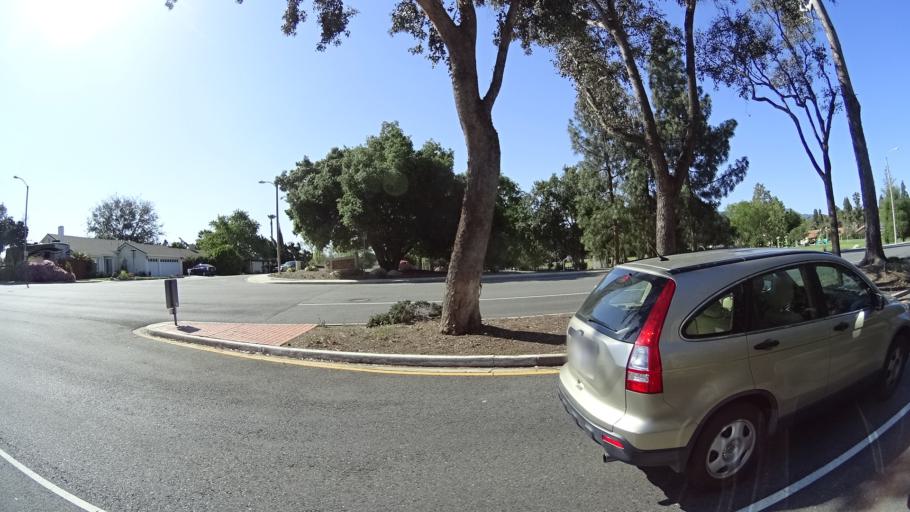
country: US
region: California
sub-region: Ventura County
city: Moorpark
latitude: 34.2263
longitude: -118.8727
